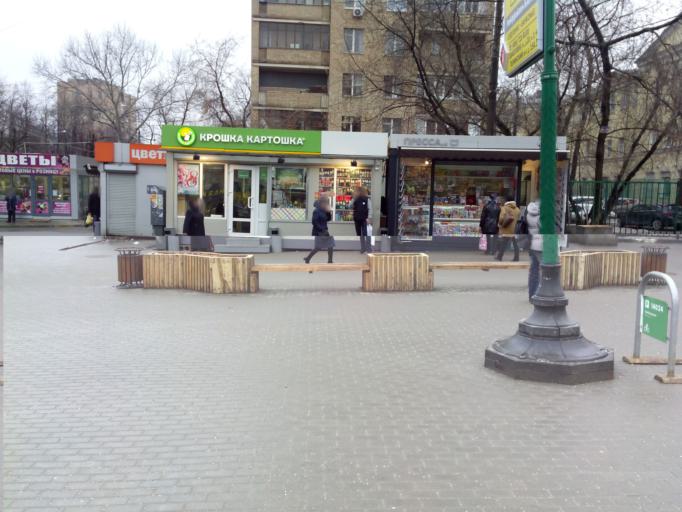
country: RU
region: Moscow
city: Zamoskvorech'ye
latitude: 55.7187
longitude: 37.6086
